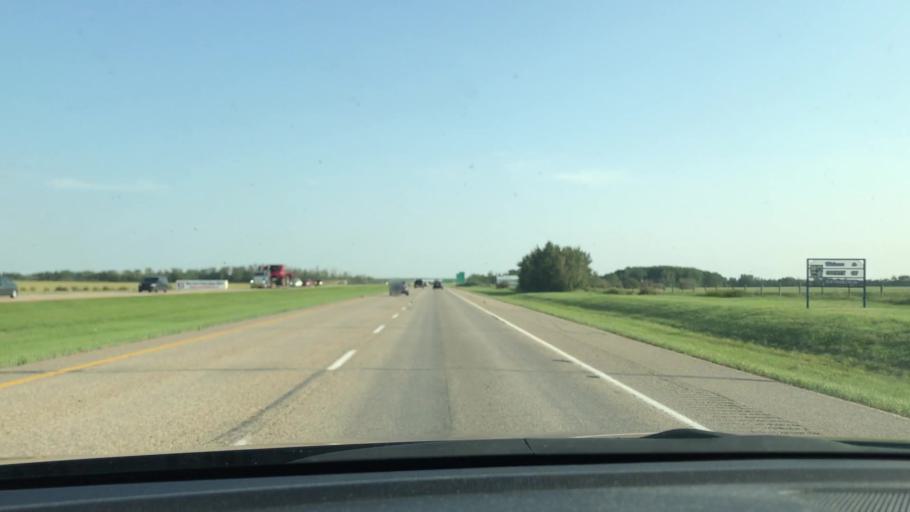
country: CA
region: Alberta
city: Millet
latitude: 53.1053
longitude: -113.5984
